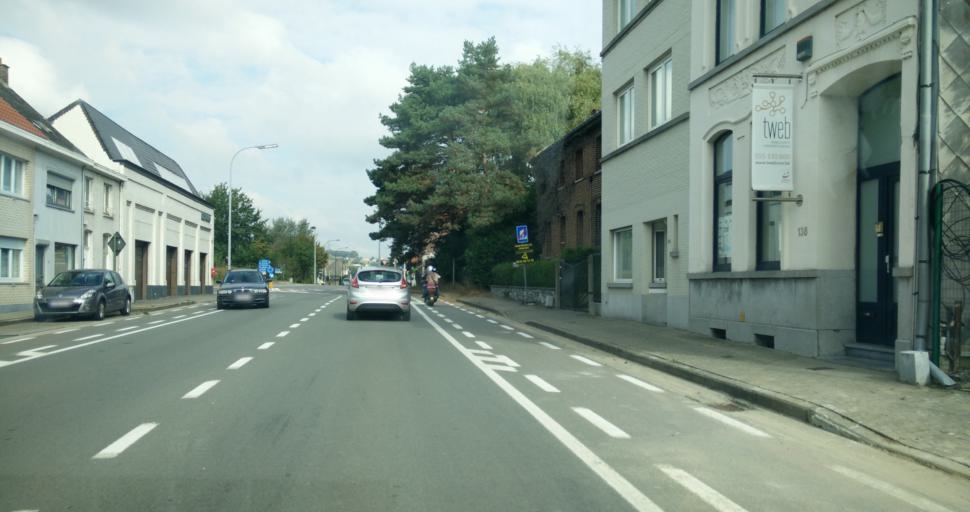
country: BE
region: Flanders
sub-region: Provincie Oost-Vlaanderen
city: Ronse
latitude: 50.7393
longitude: 3.5884
